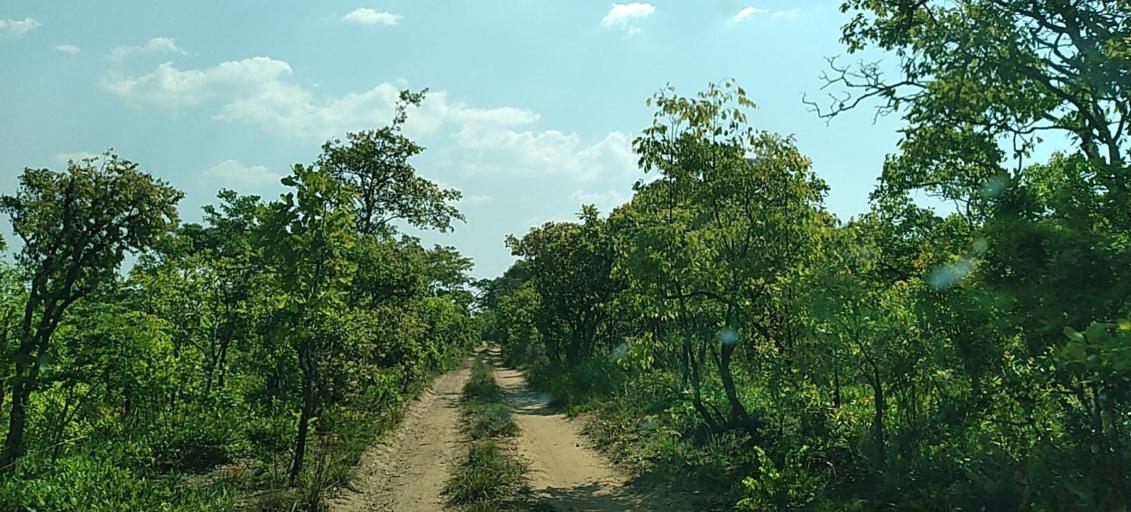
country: CD
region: Katanga
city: Kolwezi
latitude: -11.2651
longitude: 25.0011
